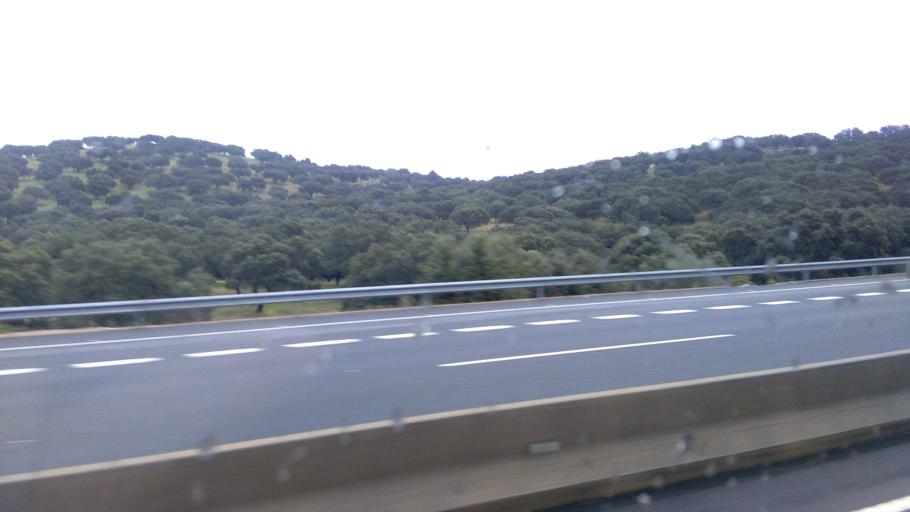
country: ES
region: Extremadura
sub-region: Provincia de Caceres
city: Casas de Miravete
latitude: 39.7602
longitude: -5.7332
